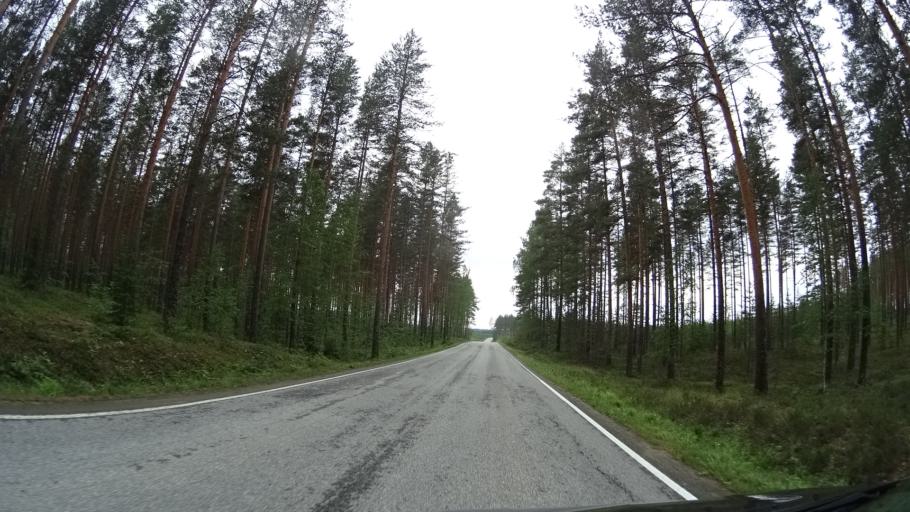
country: FI
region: Southern Savonia
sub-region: Savonlinna
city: Punkaharju
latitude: 61.7493
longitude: 29.4837
